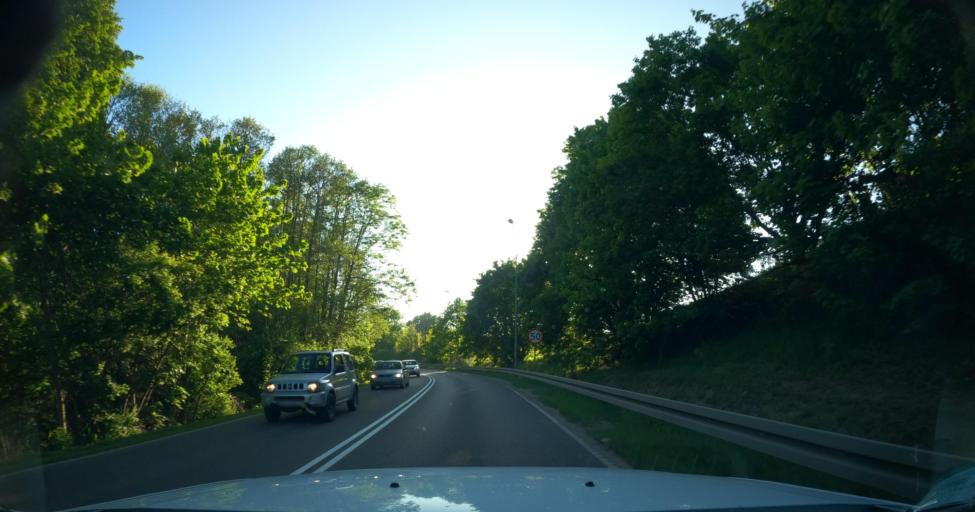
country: PL
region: Pomeranian Voivodeship
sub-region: Powiat kartuski
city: Zukowo
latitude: 54.3403
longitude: 18.3474
